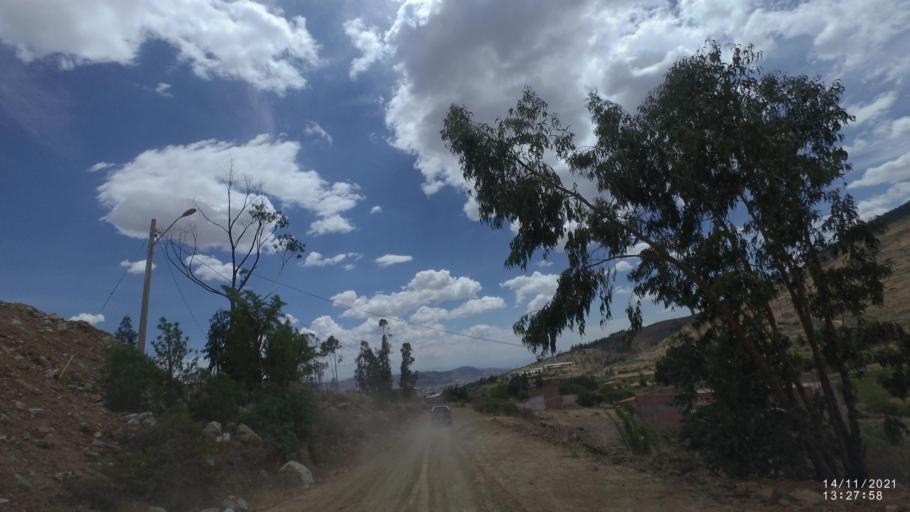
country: BO
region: Cochabamba
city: Colomi
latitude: -17.3846
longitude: -65.9826
